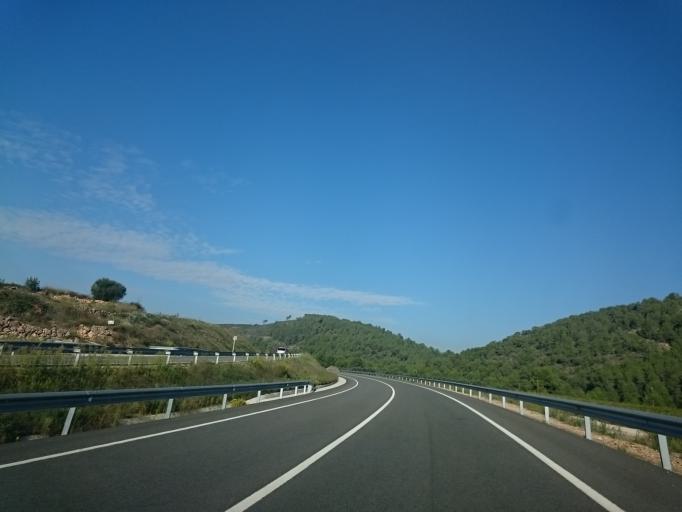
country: ES
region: Catalonia
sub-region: Provincia de Tarragona
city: la Bisbal del Penedes
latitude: 41.2685
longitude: 1.4835
